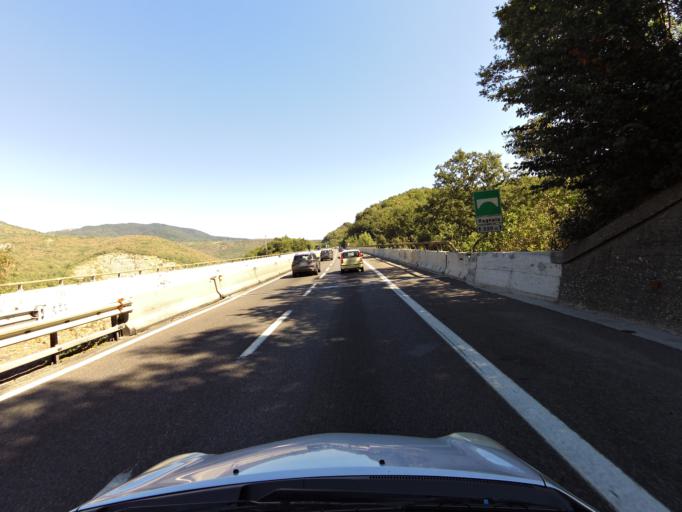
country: IT
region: Tuscany
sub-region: Province of Florence
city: Carraia
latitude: 43.8996
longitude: 11.1929
